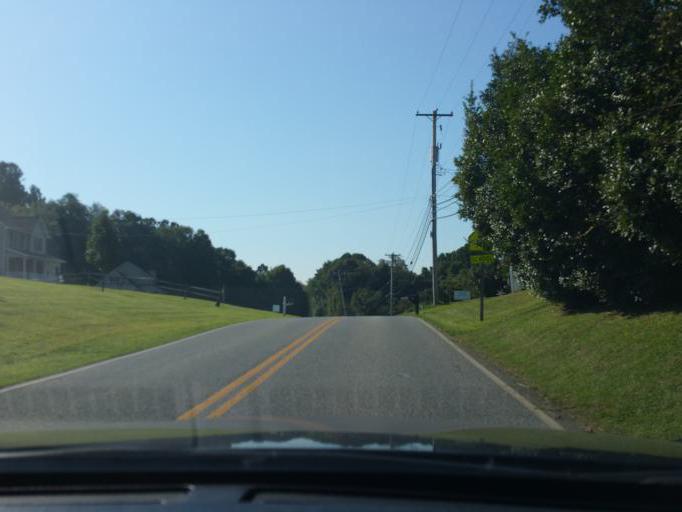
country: US
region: Maryland
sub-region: Cecil County
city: Rising Sun
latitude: 39.6761
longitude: -76.1581
